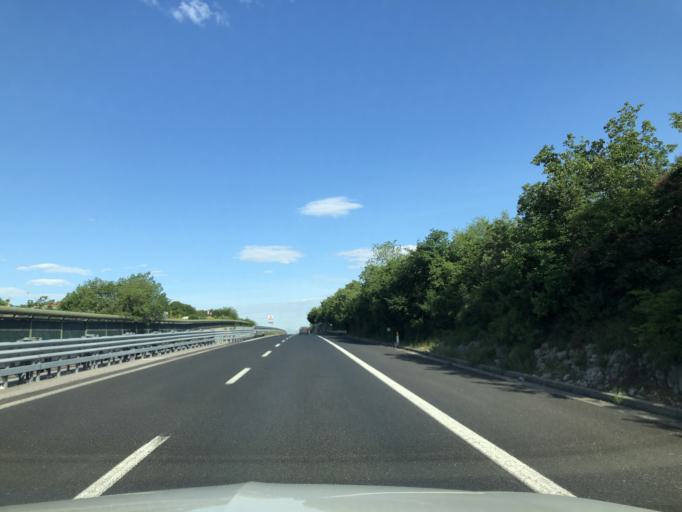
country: IT
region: Friuli Venezia Giulia
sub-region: Provincia di Trieste
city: Aurisina Cave
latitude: 45.7622
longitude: 13.6632
